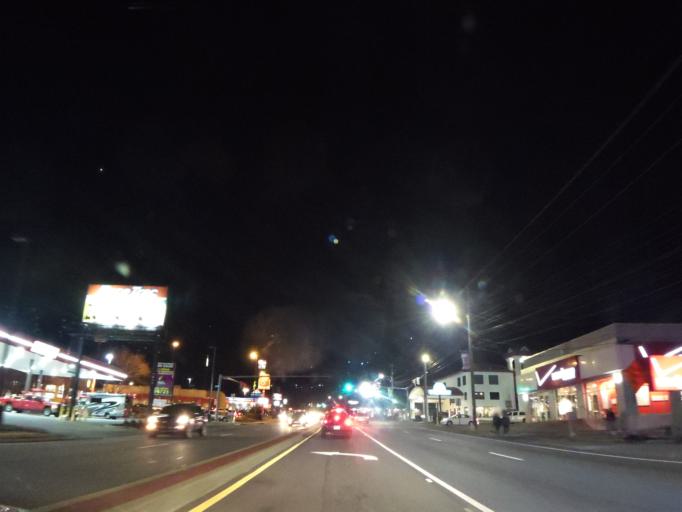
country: US
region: Georgia
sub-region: Whitfield County
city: Dalton
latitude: 34.7605
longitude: -84.9963
